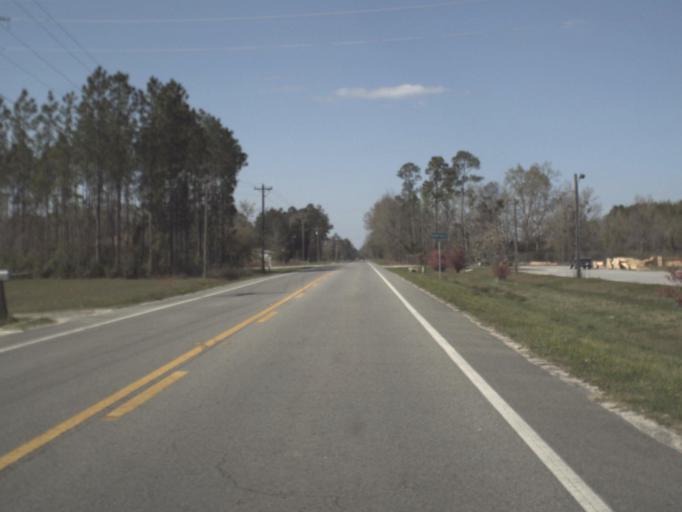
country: US
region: Florida
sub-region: Gulf County
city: Wewahitchka
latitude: 30.0417
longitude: -85.1848
